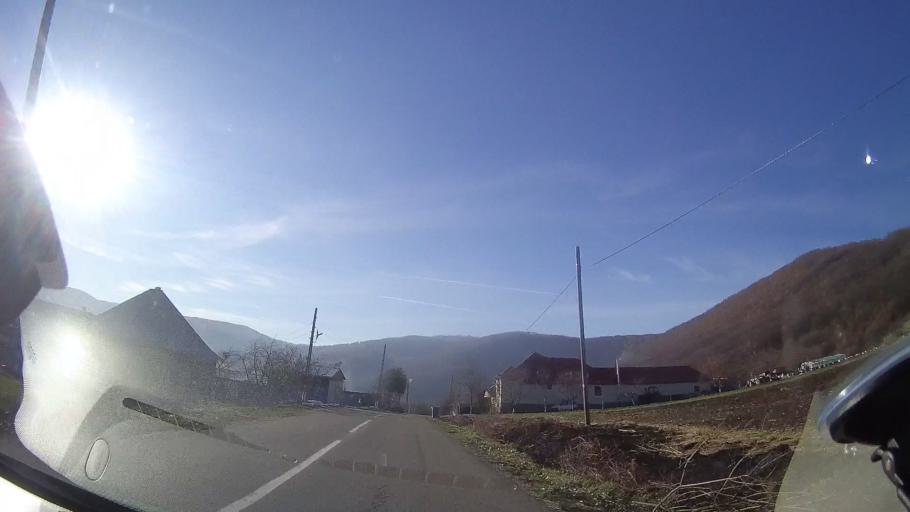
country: RO
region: Bihor
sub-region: Comuna Suncuius
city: Suncuius
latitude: 46.9575
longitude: 22.5393
